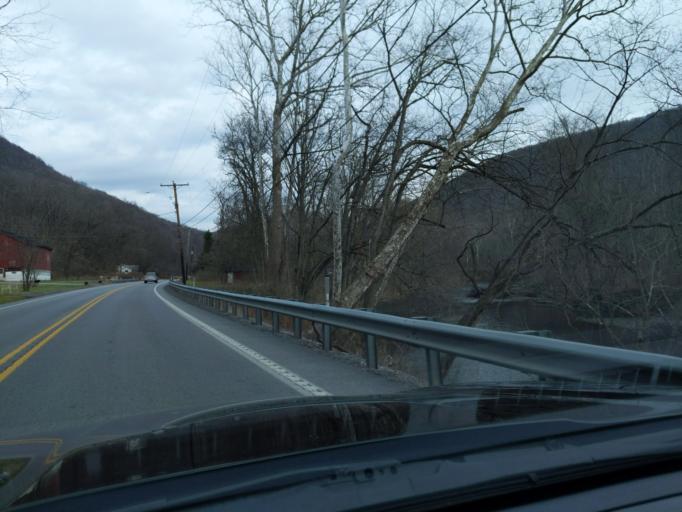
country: US
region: Pennsylvania
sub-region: Blair County
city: Williamsburg
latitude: 40.4812
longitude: -78.2603
